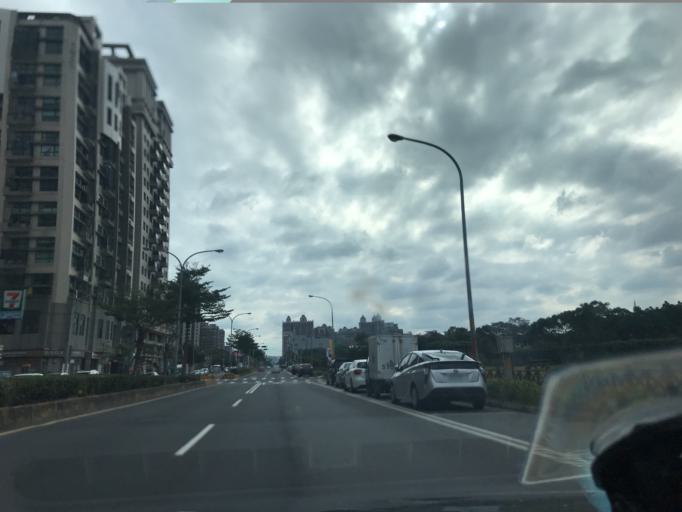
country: TW
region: Taiwan
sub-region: Hsinchu
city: Zhubei
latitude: 24.8263
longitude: 121.0248
